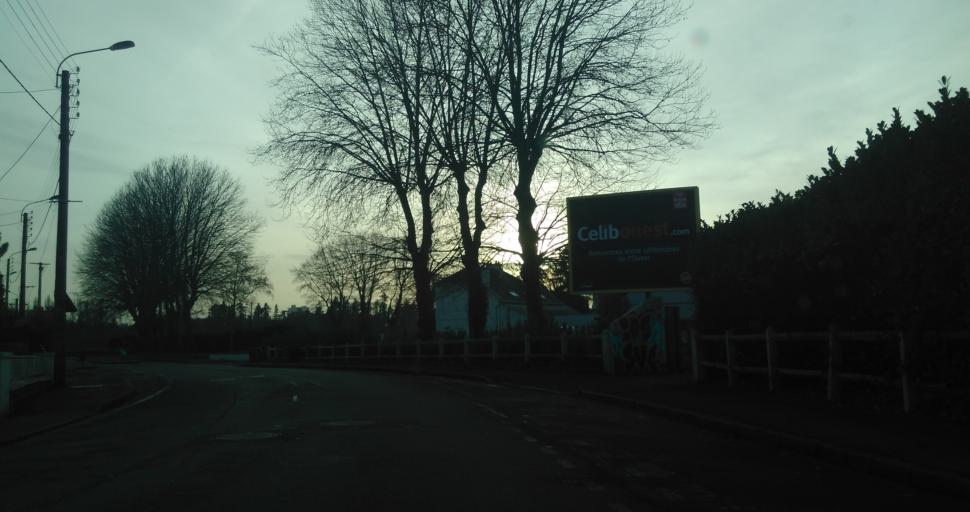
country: FR
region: Brittany
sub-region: Departement d'Ille-et-Vilaine
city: Rennes
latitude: 48.1305
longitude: -1.6736
